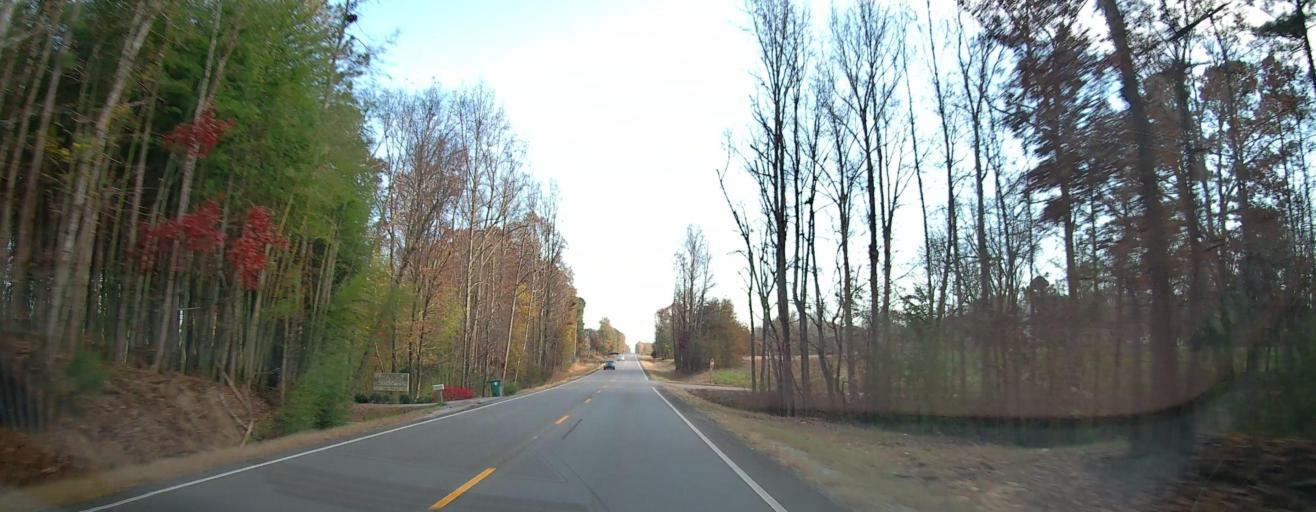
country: US
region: Alabama
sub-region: Marshall County
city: Arab
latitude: 34.2802
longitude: -86.5836
